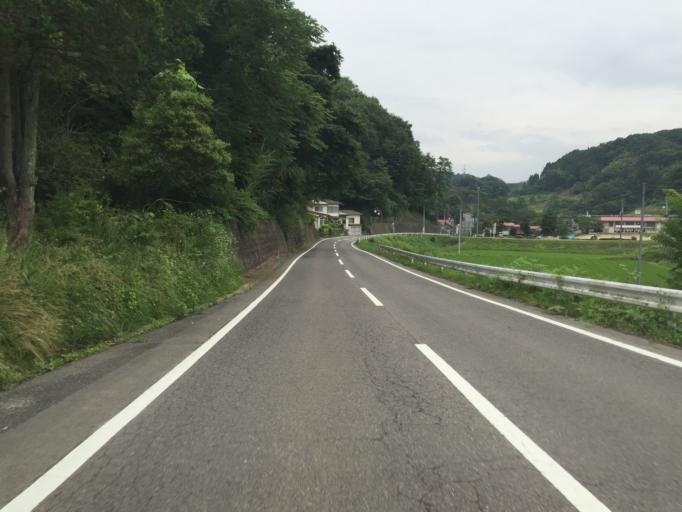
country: JP
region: Fukushima
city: Nihommatsu
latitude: 37.6211
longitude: 140.5585
